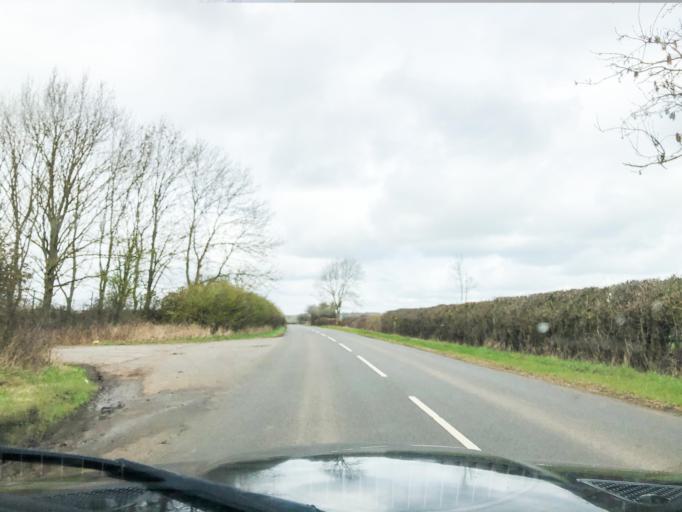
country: GB
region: England
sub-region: Warwickshire
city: Harbury
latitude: 52.1504
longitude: -1.4386
